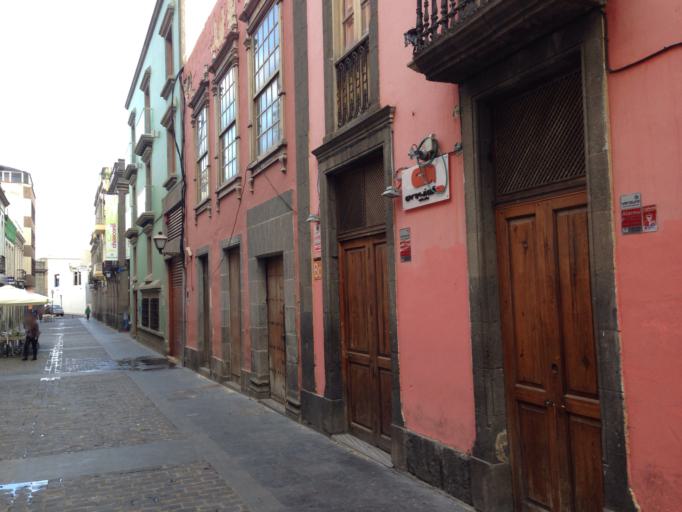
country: ES
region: Canary Islands
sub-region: Provincia de Las Palmas
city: Las Palmas de Gran Canaria
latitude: 28.1020
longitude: -15.4146
